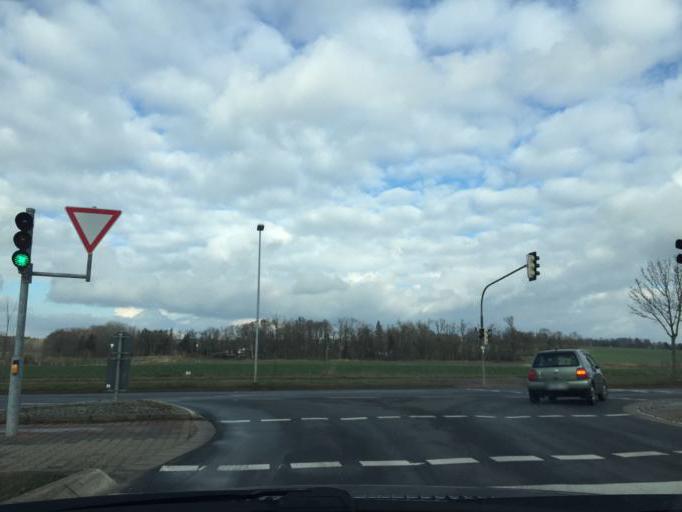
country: DE
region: Saxony
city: Radeberg
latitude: 51.1246
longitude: 13.9315
